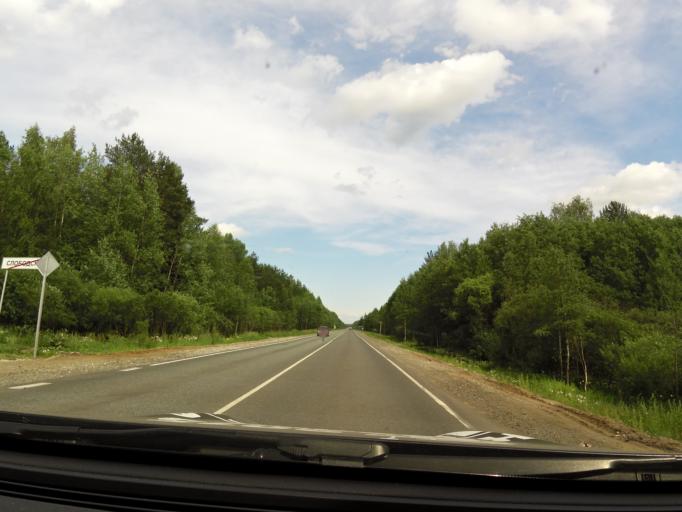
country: RU
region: Kirov
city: Slobodskoy
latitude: 58.7253
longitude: 50.2044
